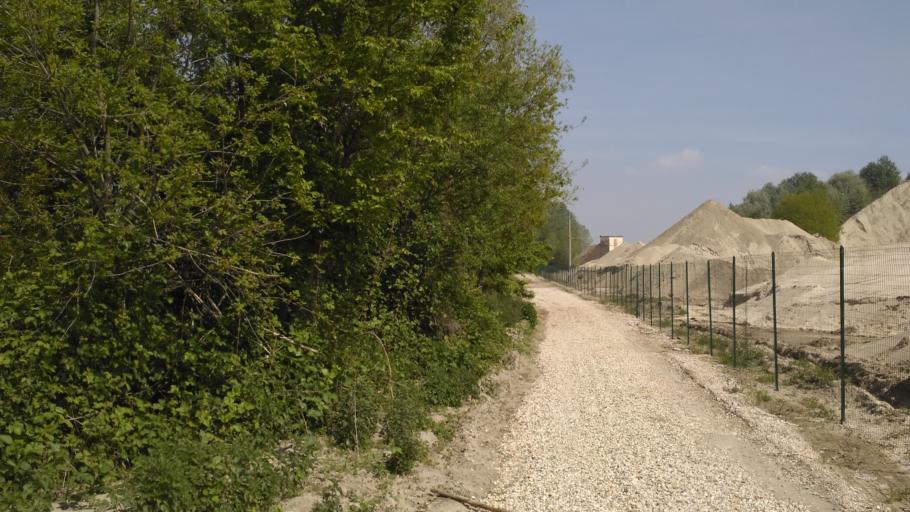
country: IT
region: Piedmont
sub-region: Provincia di Cuneo
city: Casalgrasso
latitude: 44.8238
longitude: 7.6151
